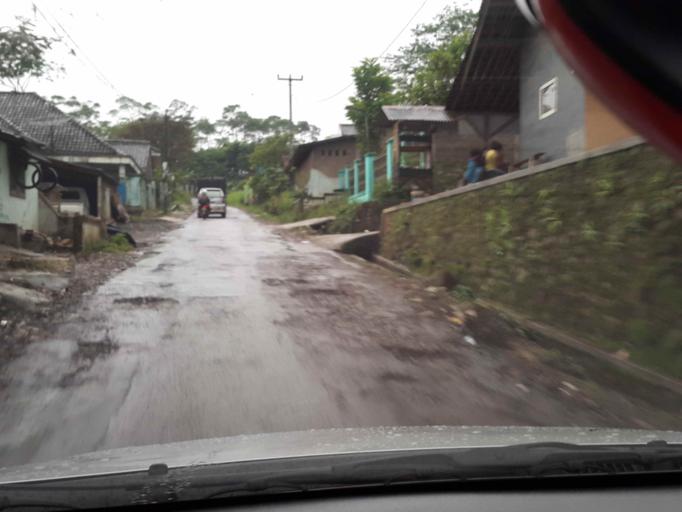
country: ID
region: West Java
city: Sukabumi
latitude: -6.9167
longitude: 106.8603
